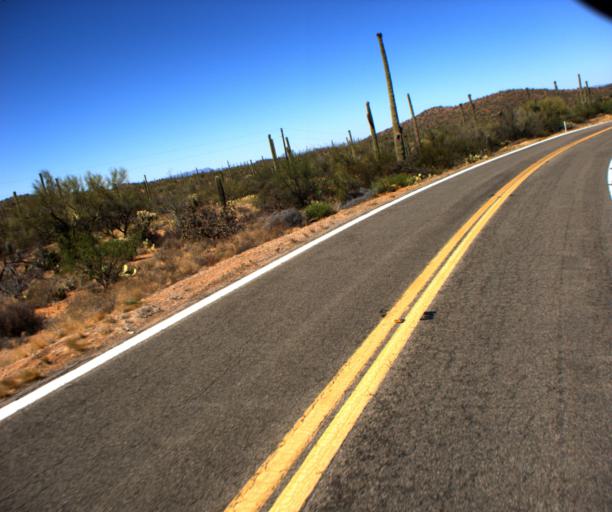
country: US
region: Arizona
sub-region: Pima County
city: Sells
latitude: 32.1738
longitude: -112.2013
